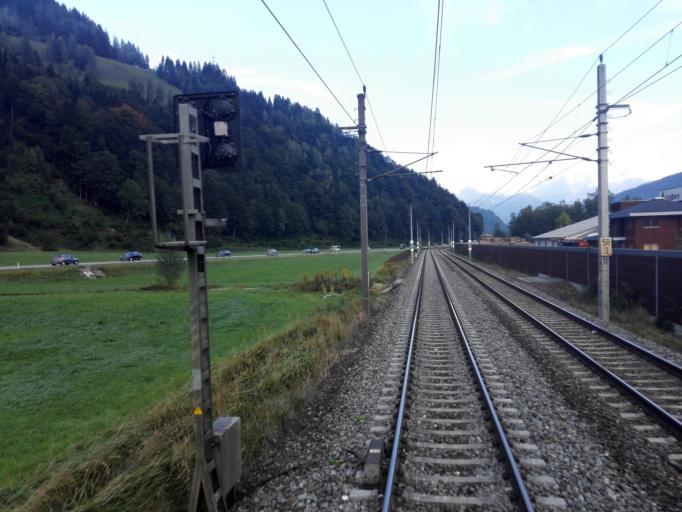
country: AT
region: Salzburg
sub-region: Politischer Bezirk Sankt Johann im Pongau
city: Sankt Johann im Pongau
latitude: 47.3725
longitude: 13.2076
